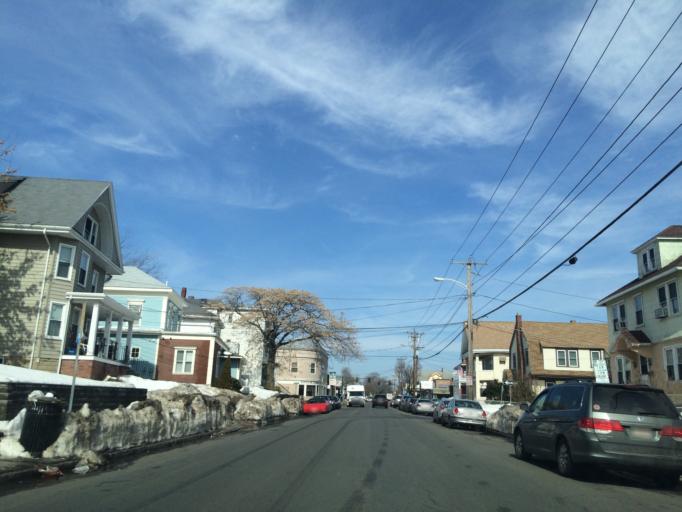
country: US
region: Massachusetts
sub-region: Middlesex County
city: Medford
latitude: 42.4036
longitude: -71.1072
